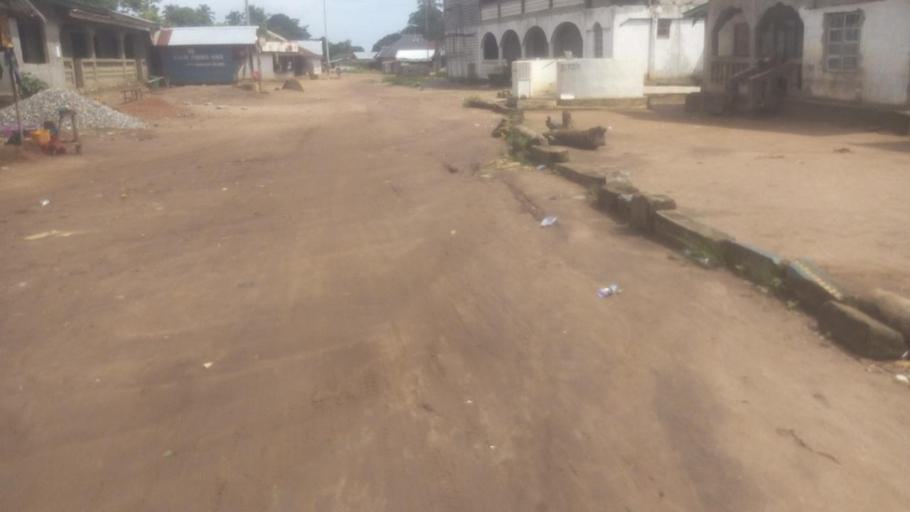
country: SL
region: Northern Province
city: Masoyila
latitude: 8.5885
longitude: -13.1986
